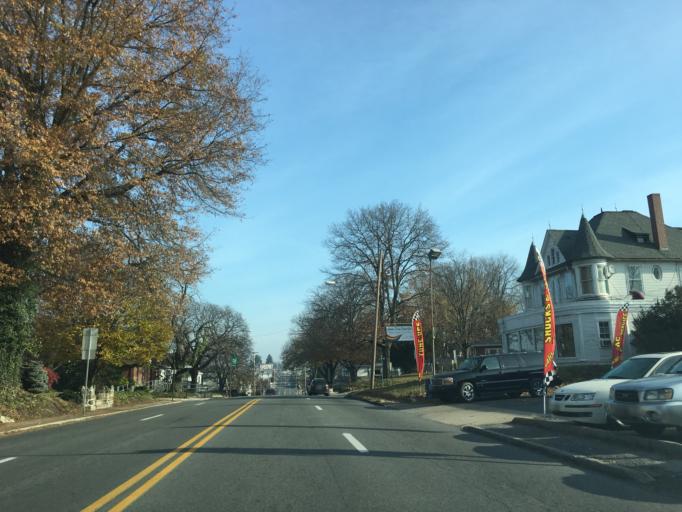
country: US
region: Pennsylvania
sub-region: Dauphin County
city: Penbrook
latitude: 40.2826
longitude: -76.8444
